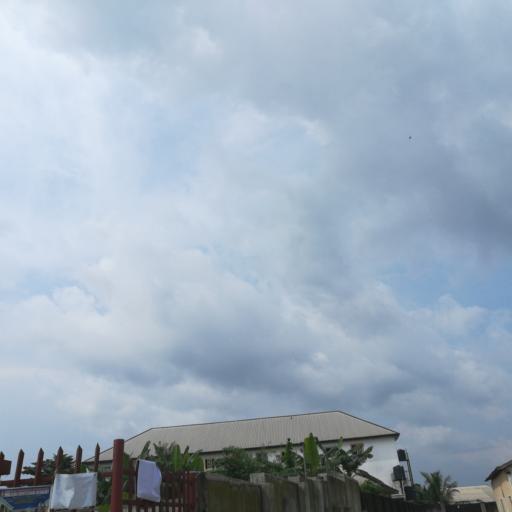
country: NG
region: Rivers
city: Port Harcourt
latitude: 4.8718
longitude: 7.0233
